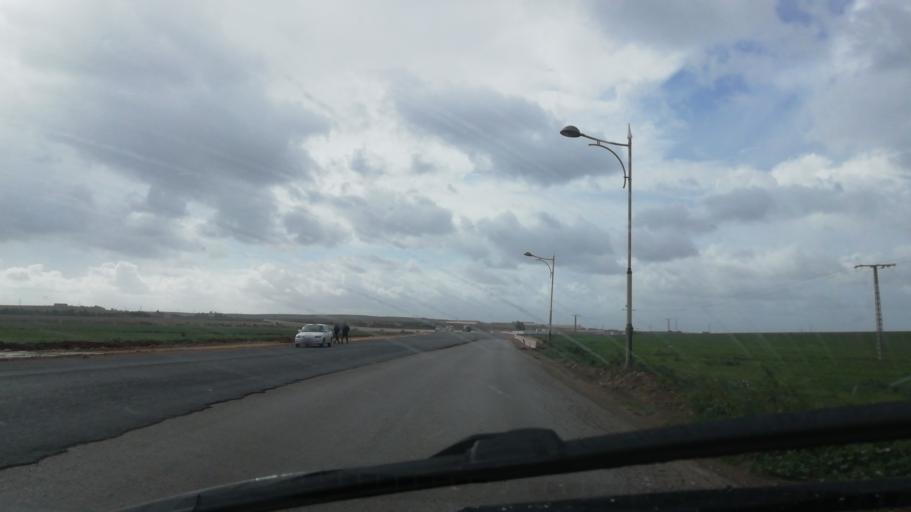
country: DZ
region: Oran
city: Sidi ech Chahmi
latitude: 35.6473
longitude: -0.5242
